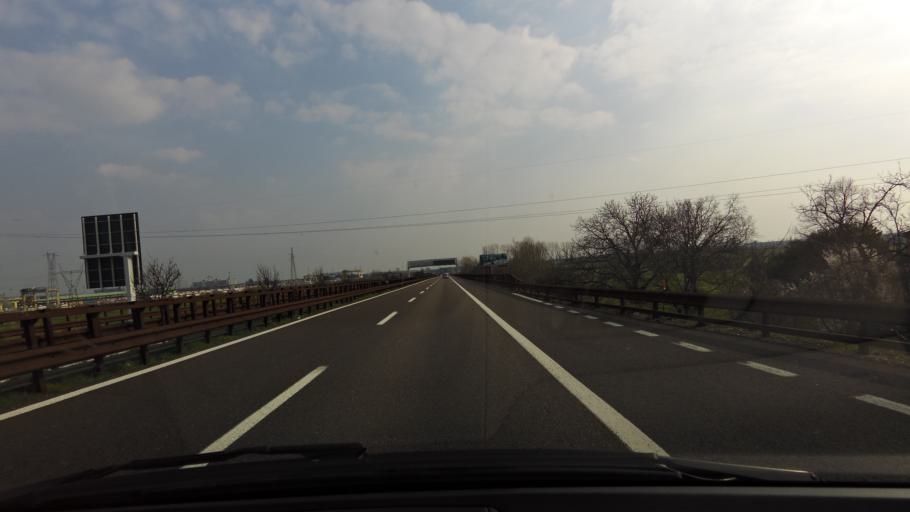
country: IT
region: Veneto
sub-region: Provincia di Verona
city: Caselle
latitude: 45.4249
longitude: 10.9106
